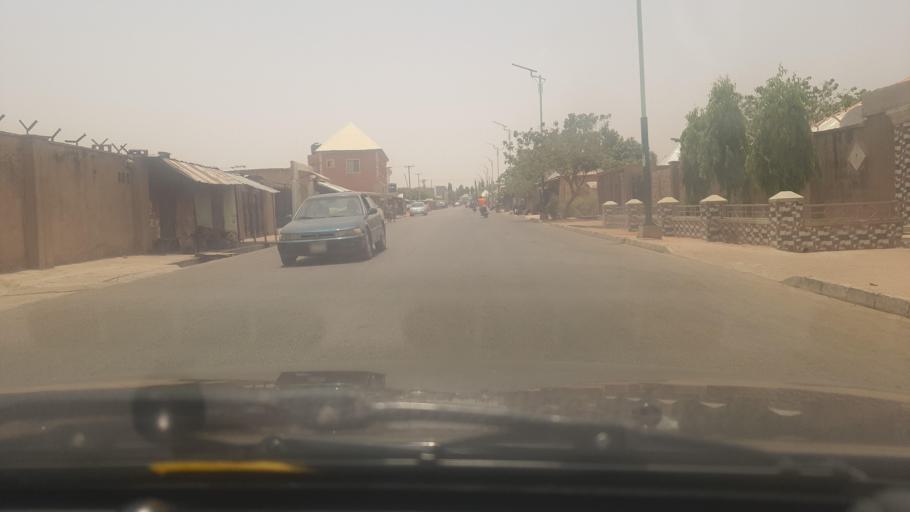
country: NG
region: Gombe
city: Gombe
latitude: 10.2988
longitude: 11.1506
